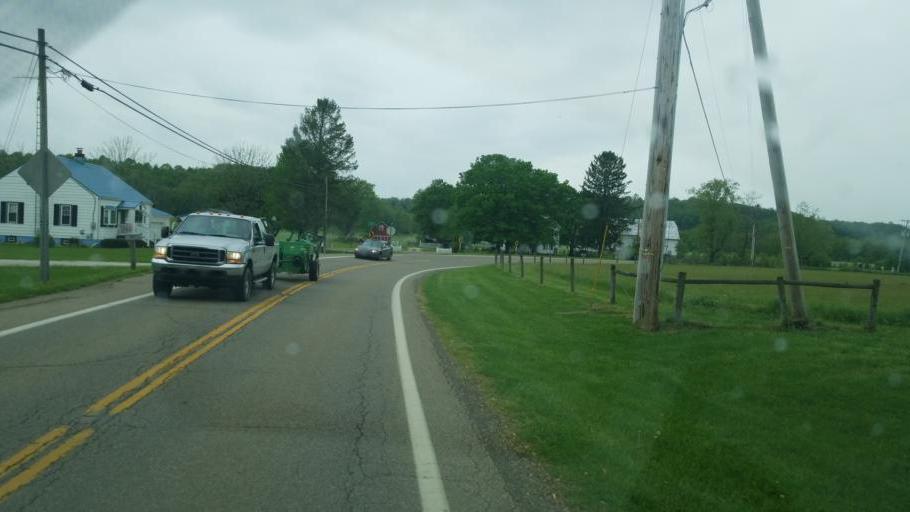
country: US
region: Ohio
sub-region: Coshocton County
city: West Lafayette
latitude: 40.2107
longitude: -81.7239
